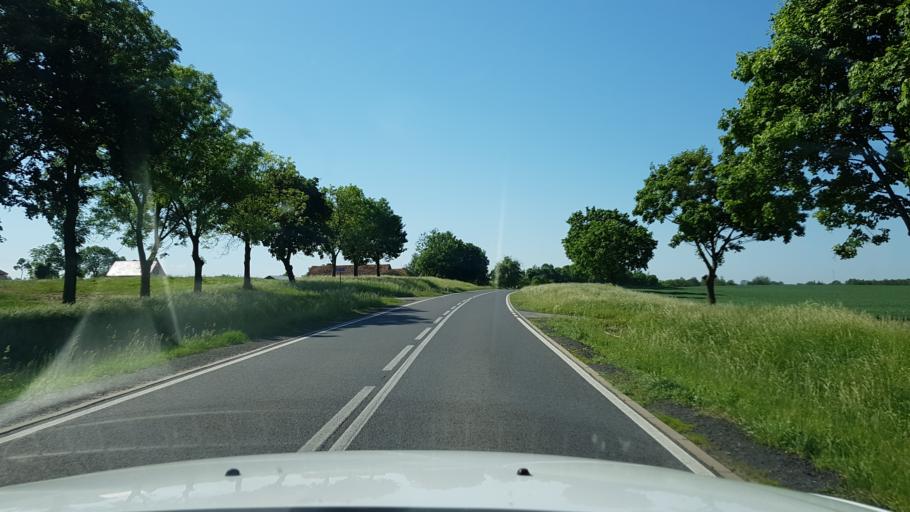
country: PL
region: West Pomeranian Voivodeship
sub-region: Powiat gryfinski
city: Mieszkowice
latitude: 52.8046
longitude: 14.4990
